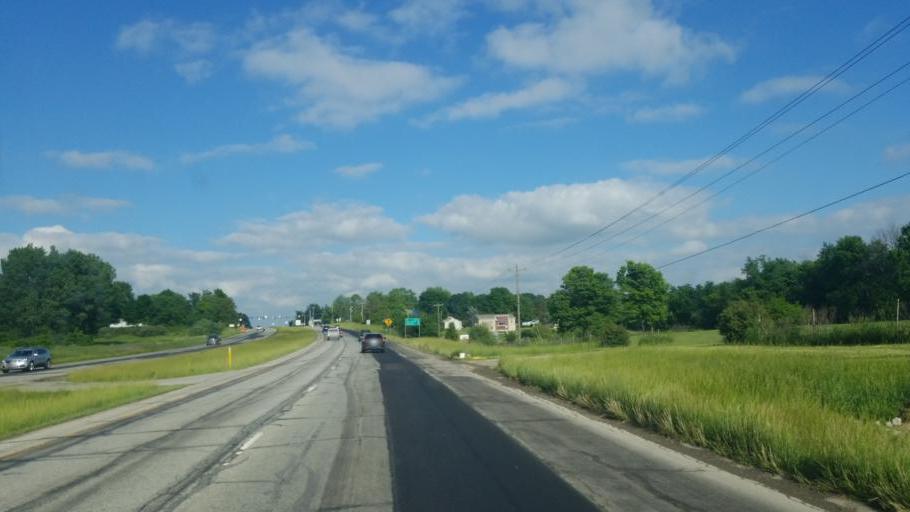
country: US
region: Indiana
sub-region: Kosciusko County
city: Pierceton
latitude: 41.1816
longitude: -85.6312
